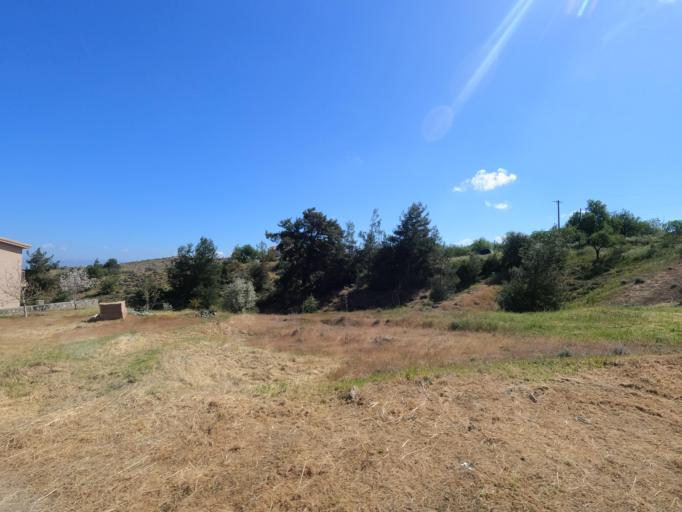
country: CY
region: Lefkosia
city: Peristerona
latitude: 35.0525
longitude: 33.0546
